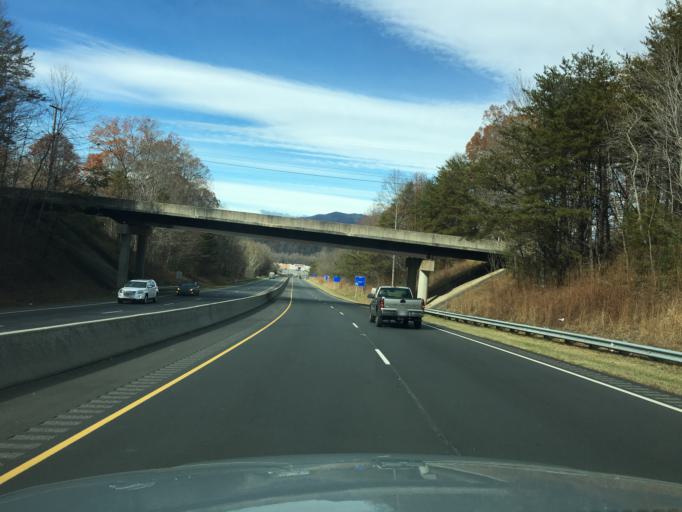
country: US
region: North Carolina
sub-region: McDowell County
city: Marion
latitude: 35.6984
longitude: -82.0309
